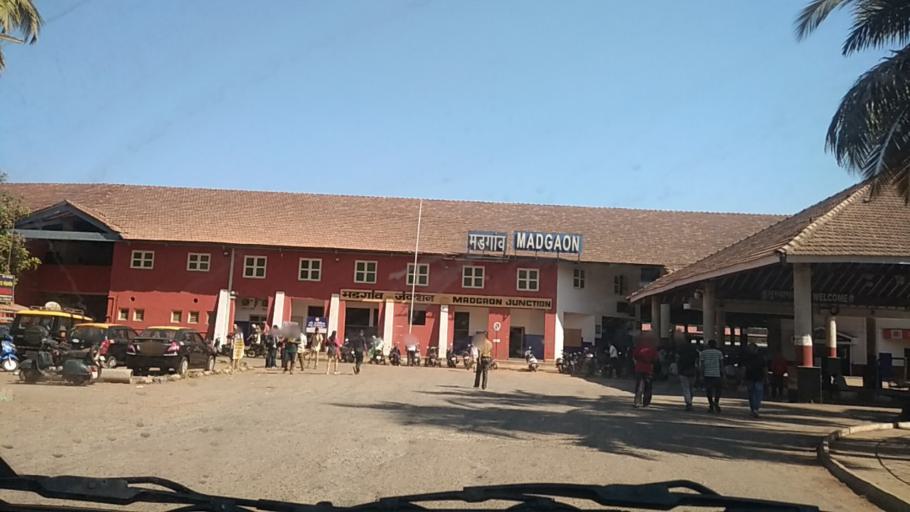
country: IN
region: Goa
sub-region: South Goa
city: Madgaon
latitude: 15.2671
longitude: 73.9708
